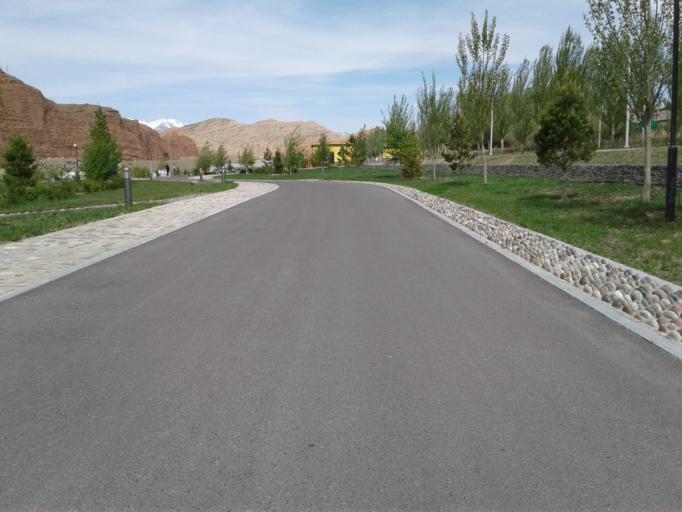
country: KG
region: Naryn
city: Naryn
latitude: 41.4286
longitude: 75.9029
